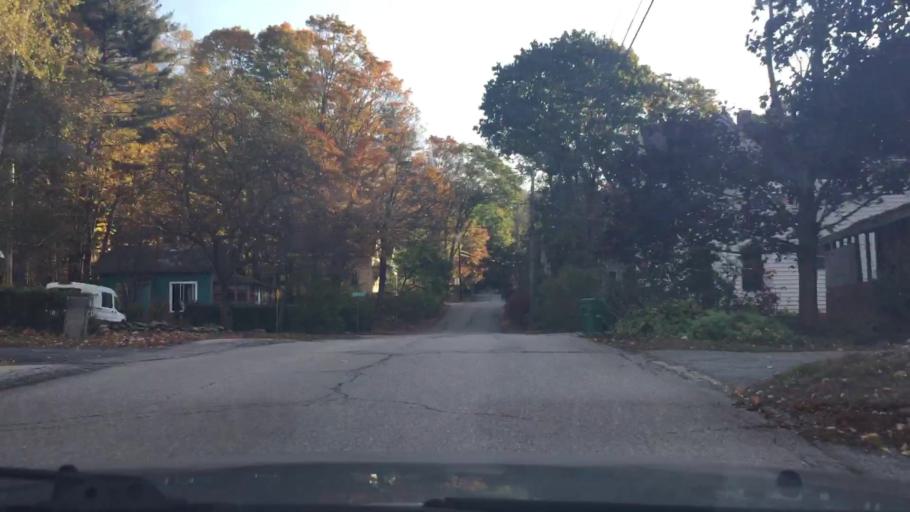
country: US
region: New Hampshire
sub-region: Cheshire County
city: Keene
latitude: 42.9450
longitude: -72.2679
